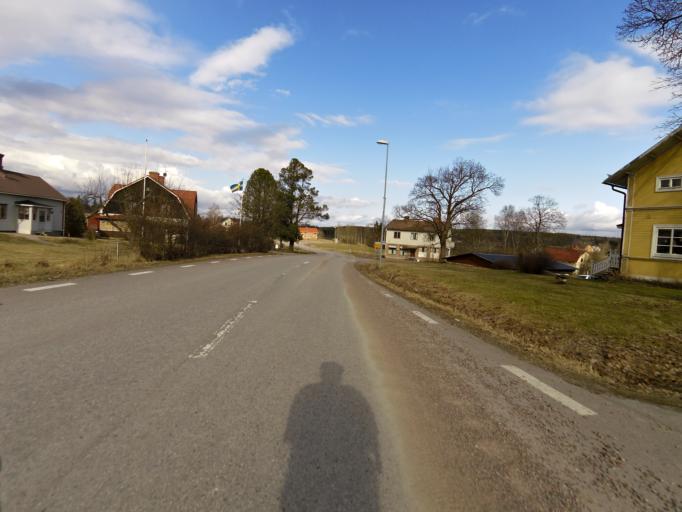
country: SE
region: Dalarna
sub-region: Avesta Kommun
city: Horndal
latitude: 60.4518
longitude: 16.4512
